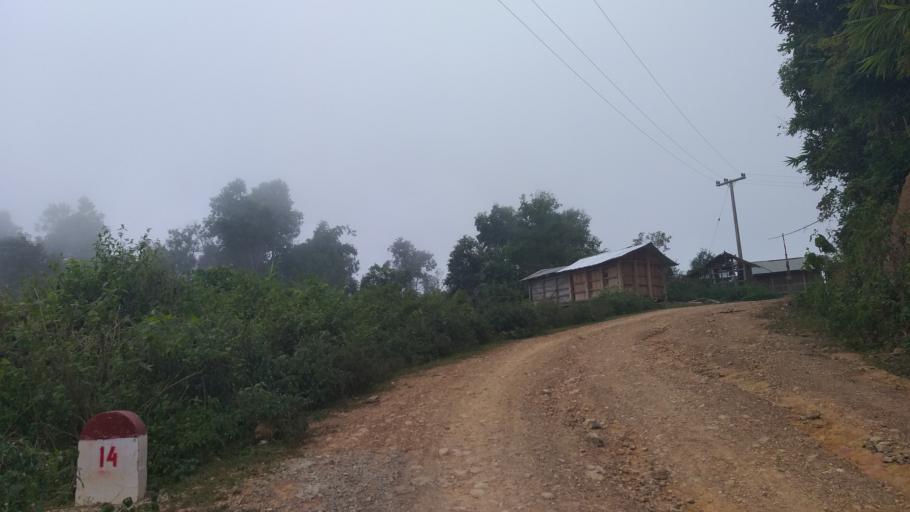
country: LA
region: Phongsali
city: Khoa
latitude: 21.2934
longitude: 102.6385
